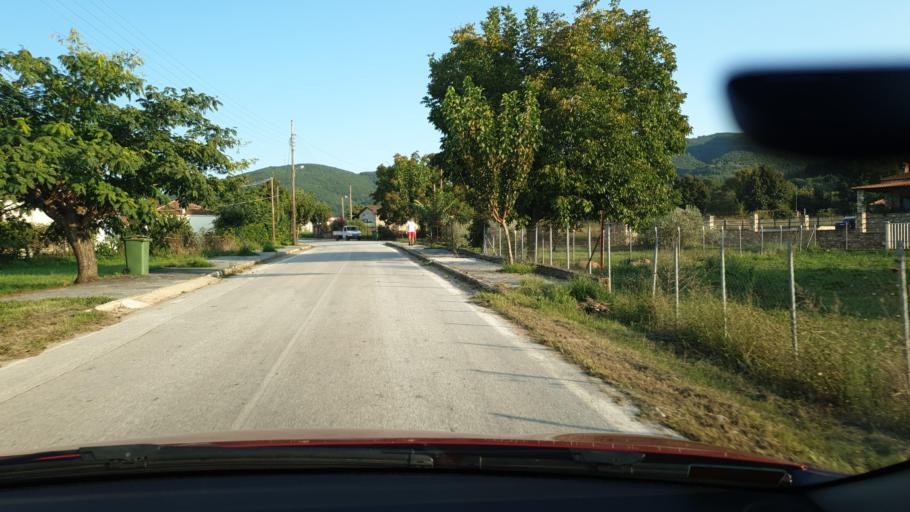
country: GR
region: Central Macedonia
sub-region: Nomos Chalkidikis
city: Galatista
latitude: 40.5585
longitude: 23.2981
